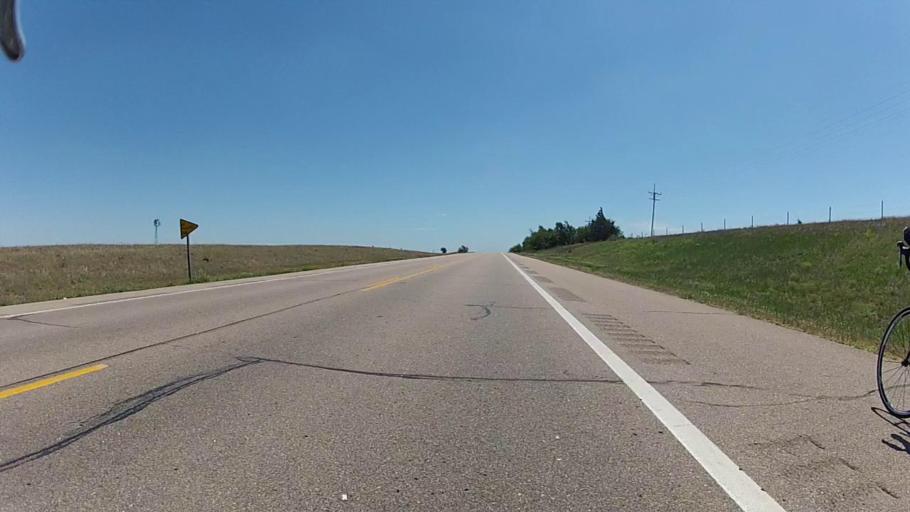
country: US
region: Kansas
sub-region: Ford County
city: Dodge City
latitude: 37.7068
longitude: -100.1317
